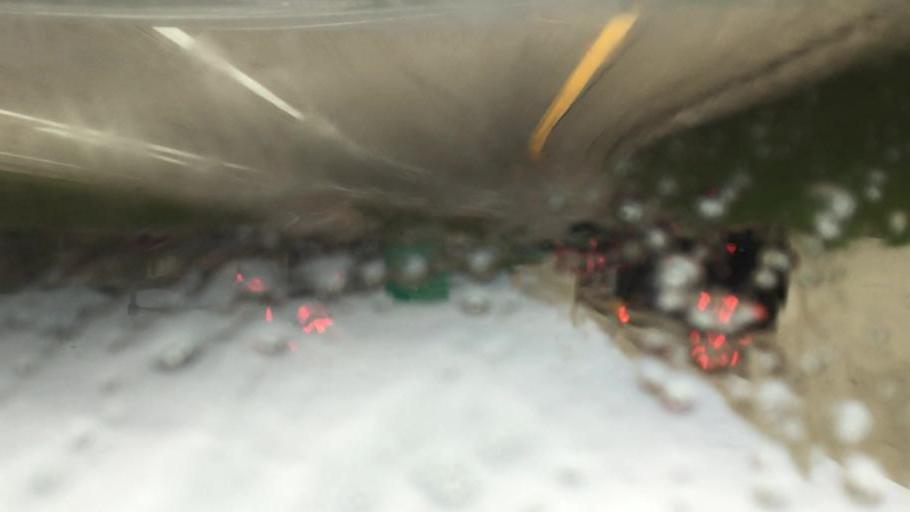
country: US
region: Michigan
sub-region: Kalamazoo County
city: Portage
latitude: 42.2371
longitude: -85.5886
